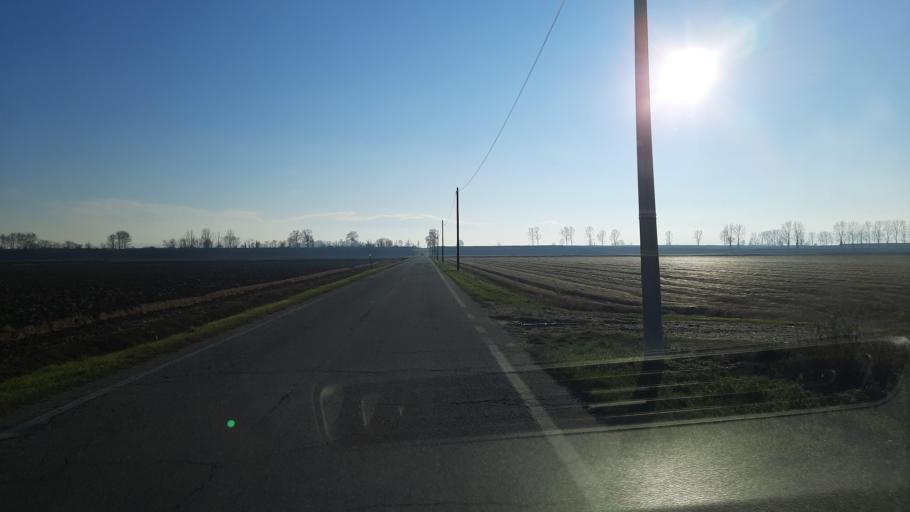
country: IT
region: Piedmont
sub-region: Provincia di Vercelli
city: Costanzana
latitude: 45.2161
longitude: 8.3637
